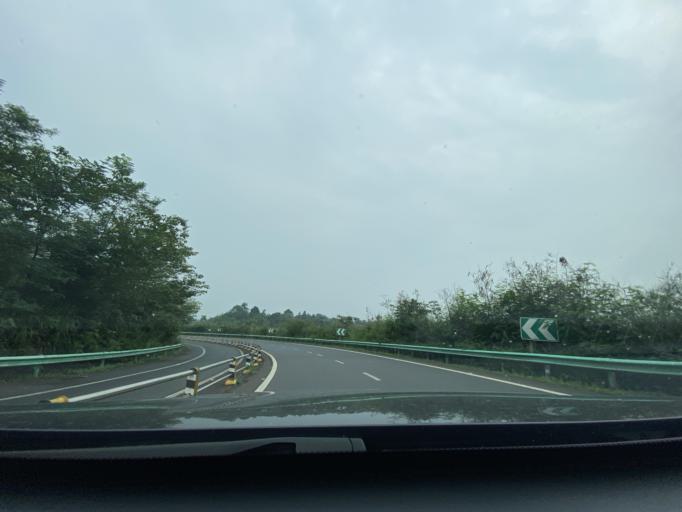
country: CN
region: Sichuan
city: Wenlin
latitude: 30.2963
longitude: 104.1249
